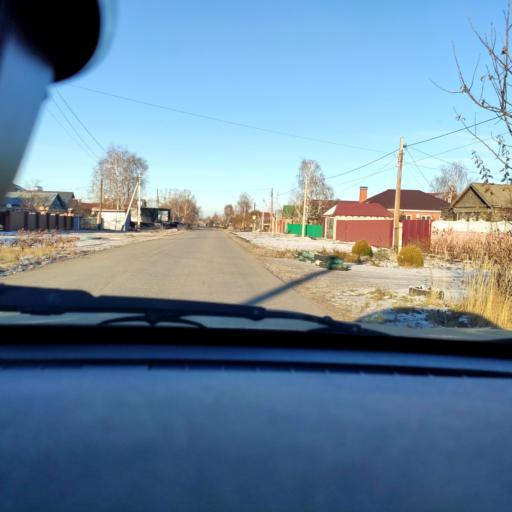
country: RU
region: Samara
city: Tol'yatti
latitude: 53.5560
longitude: 49.3974
